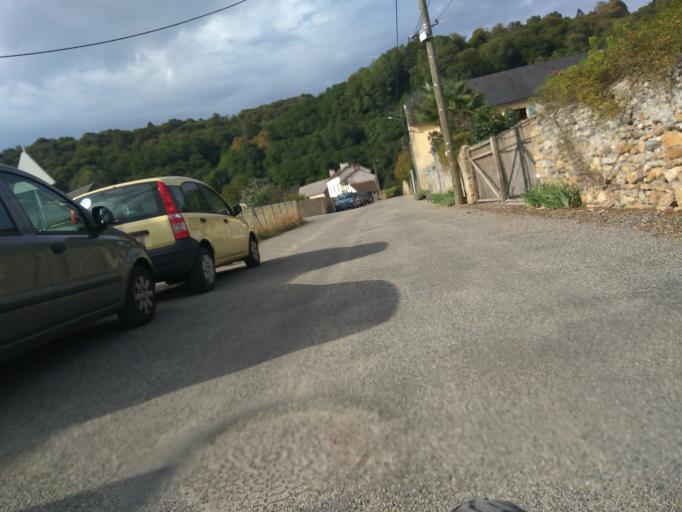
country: FR
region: Aquitaine
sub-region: Departement des Pyrenees-Atlantiques
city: Mazeres-Lezons
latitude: 43.2676
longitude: -0.3425
